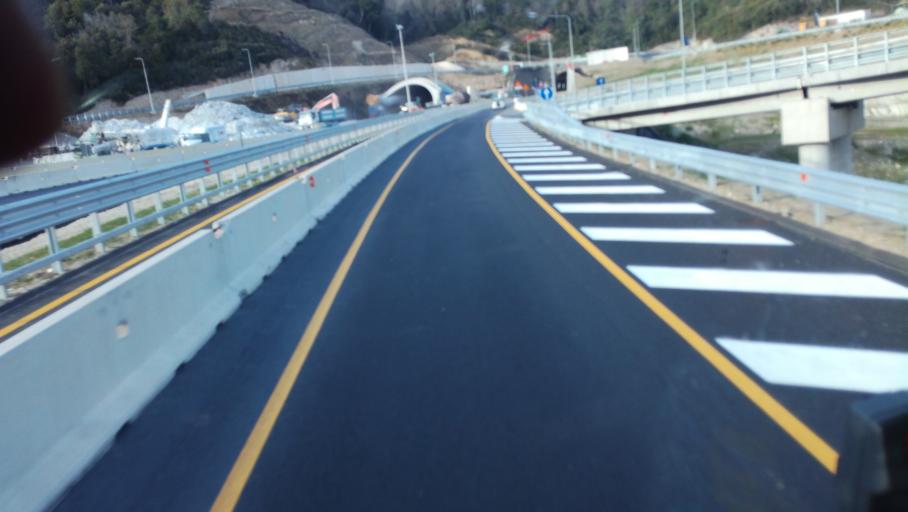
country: IT
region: Tuscany
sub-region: Provincia di Grosseto
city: Civitella Marittima
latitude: 43.0520
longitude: 11.2842
